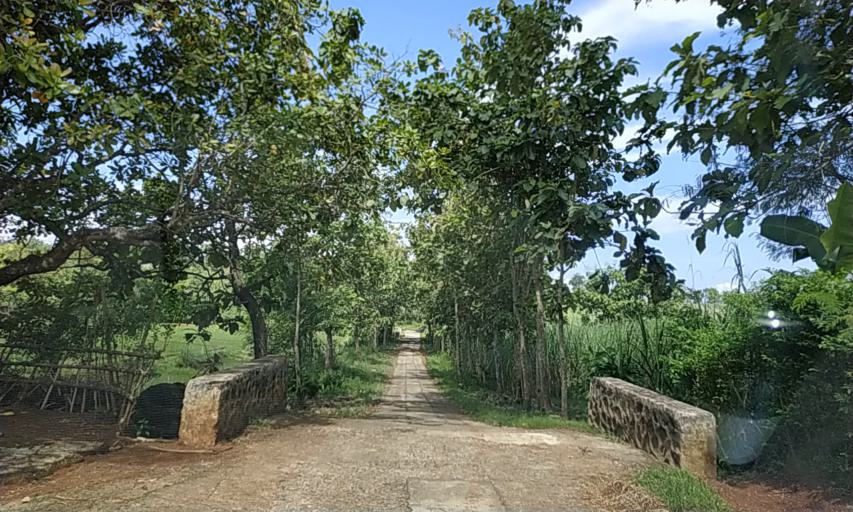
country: ID
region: Central Java
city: Selogiri
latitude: -7.8387
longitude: 110.9874
